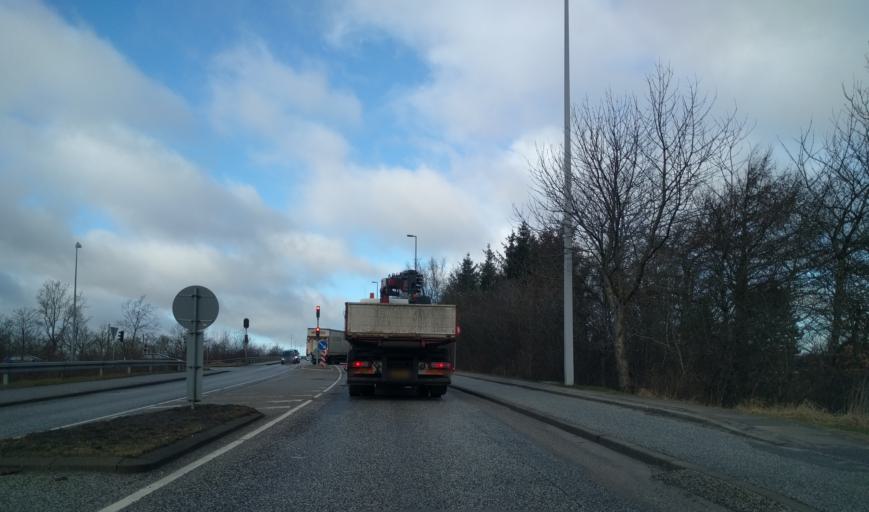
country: DK
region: North Denmark
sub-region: Alborg Kommune
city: Aalborg
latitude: 57.0131
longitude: 9.9028
